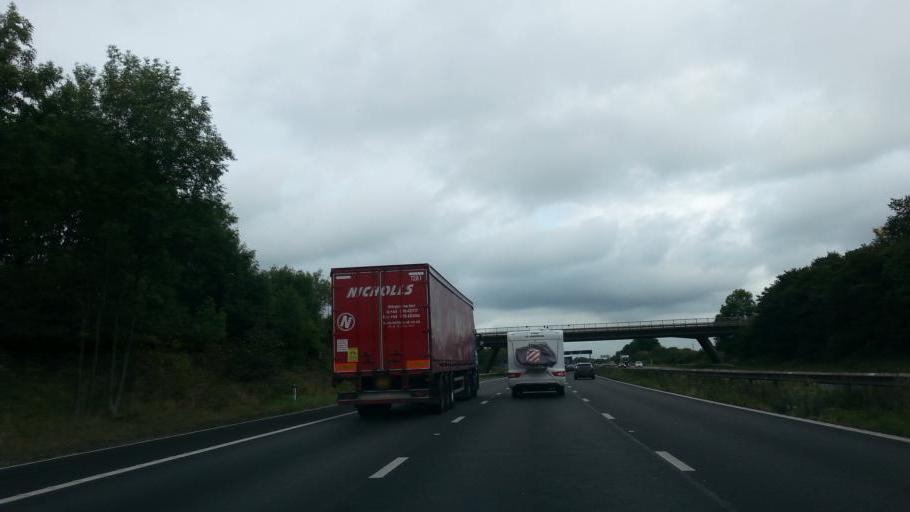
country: GB
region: England
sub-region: Leicestershire
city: Enderby
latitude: 52.5846
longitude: -1.1984
